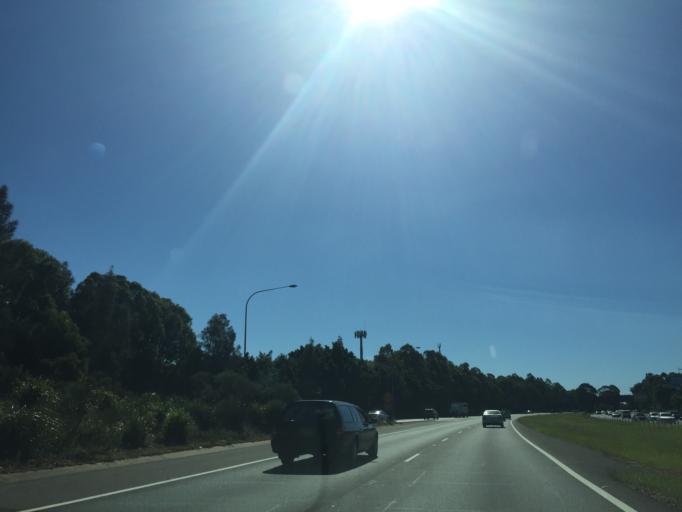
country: AU
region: New South Wales
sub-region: Strathfield
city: Homebush
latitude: -33.8568
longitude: 151.0685
